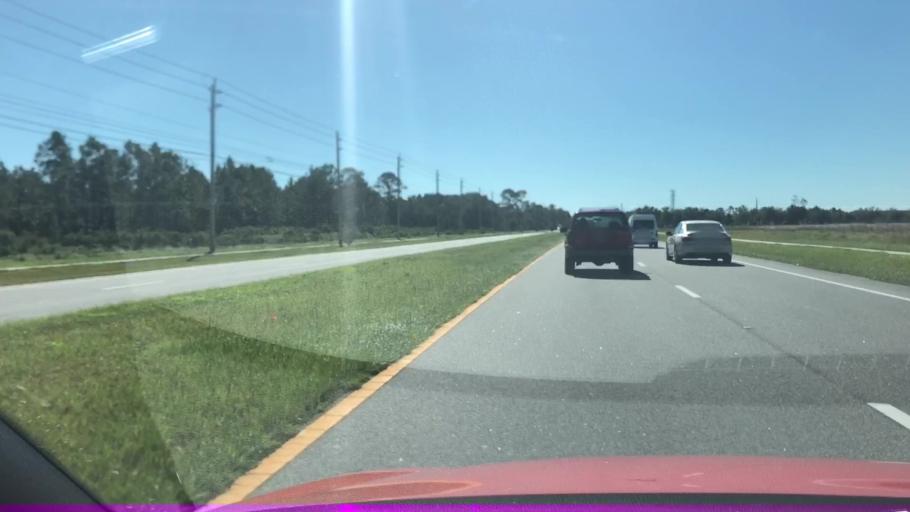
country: US
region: Florida
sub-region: Volusia County
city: Holly Hill
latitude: 29.2176
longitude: -81.0916
